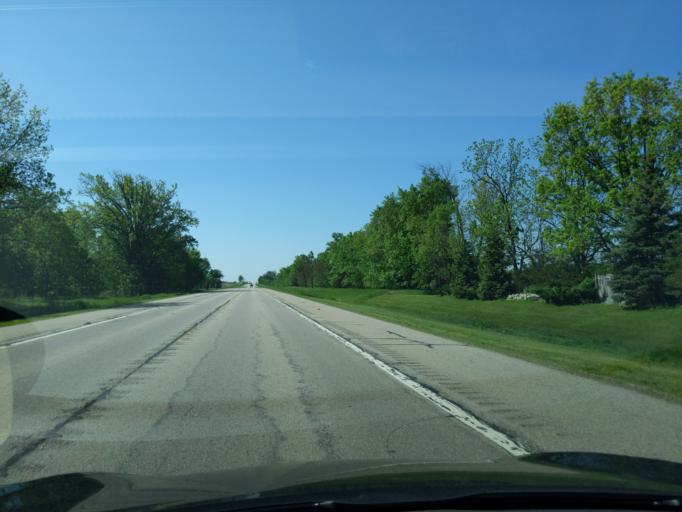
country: US
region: Michigan
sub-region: Ingham County
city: Webberville
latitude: 42.5803
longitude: -84.1927
